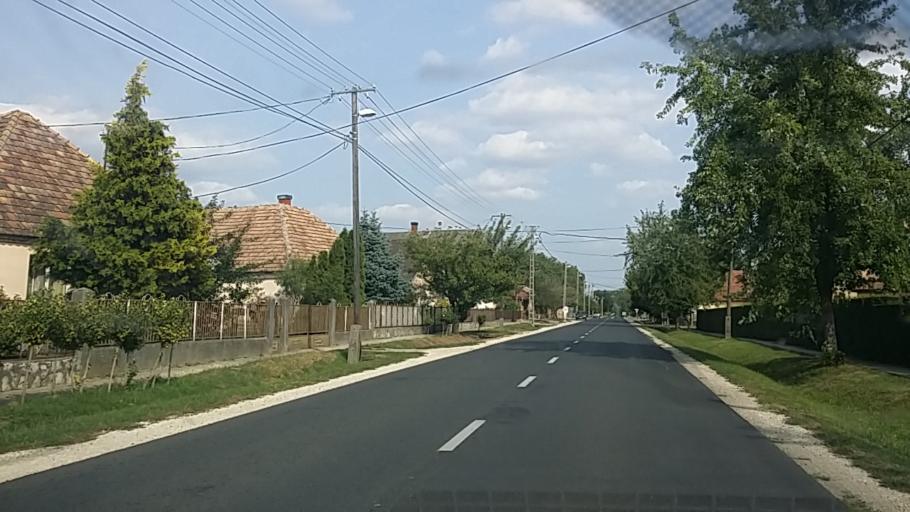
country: HU
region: Komarom-Esztergom
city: Babolna
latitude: 47.6495
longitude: 17.9279
